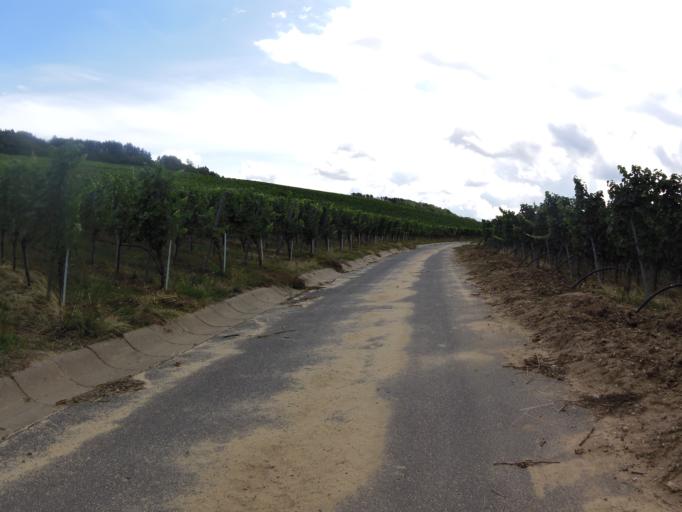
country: DE
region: Bavaria
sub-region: Regierungsbezirk Unterfranken
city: Sommerhausen
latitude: 49.6941
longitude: 10.0297
